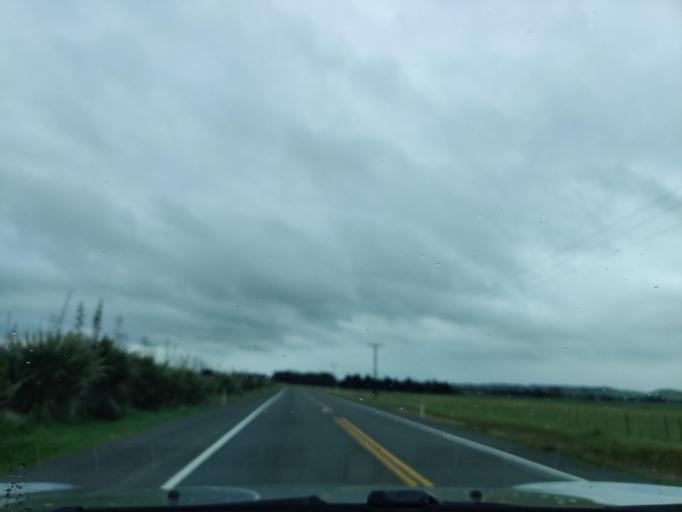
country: NZ
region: Hawke's Bay
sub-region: Hastings District
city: Hastings
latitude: -40.0017
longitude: 176.3979
